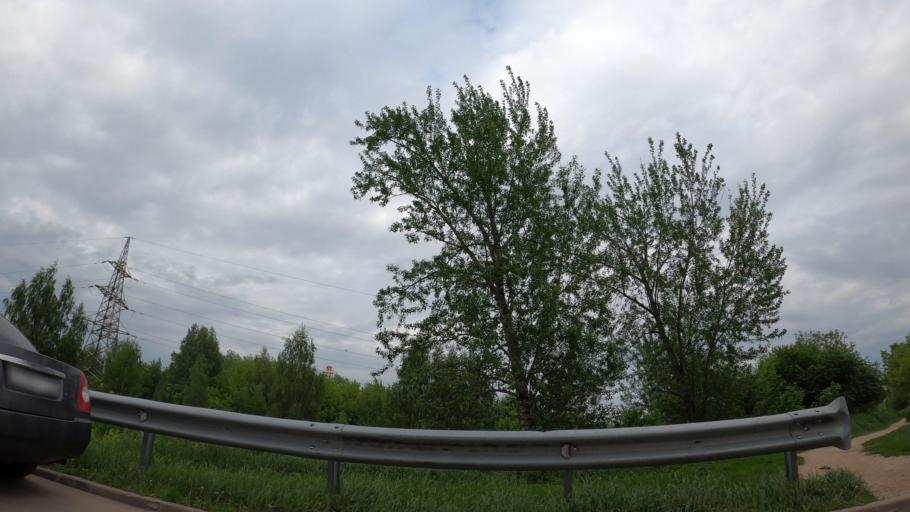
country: RU
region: Moskovskaya
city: Ivanteyevka
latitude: 55.9660
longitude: 37.9216
